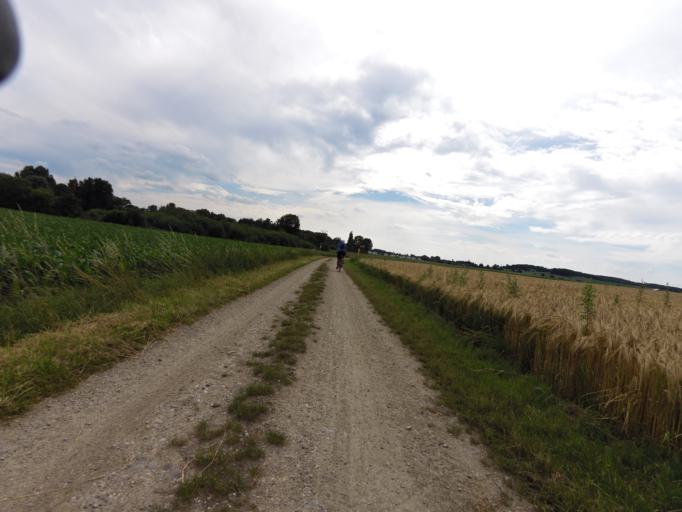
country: DE
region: Bavaria
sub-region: Upper Bavaria
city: Haimhausen
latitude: 48.3081
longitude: 11.5087
